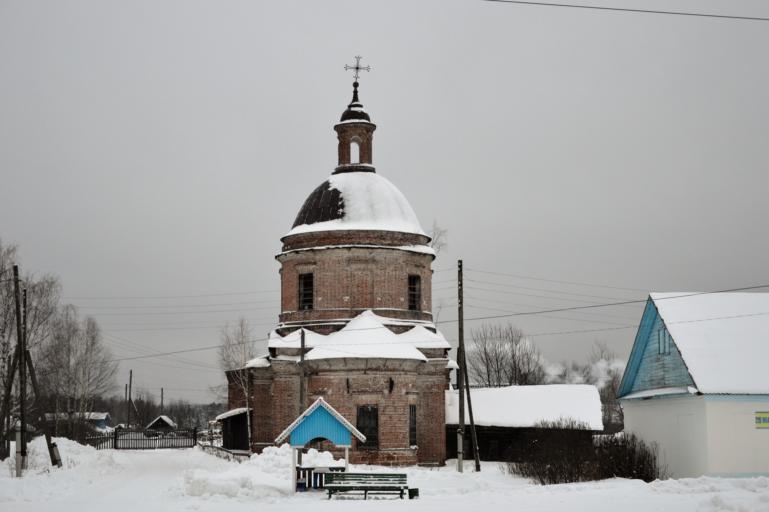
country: RU
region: Kirov
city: Darovskoy
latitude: 59.0901
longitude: 47.8339
